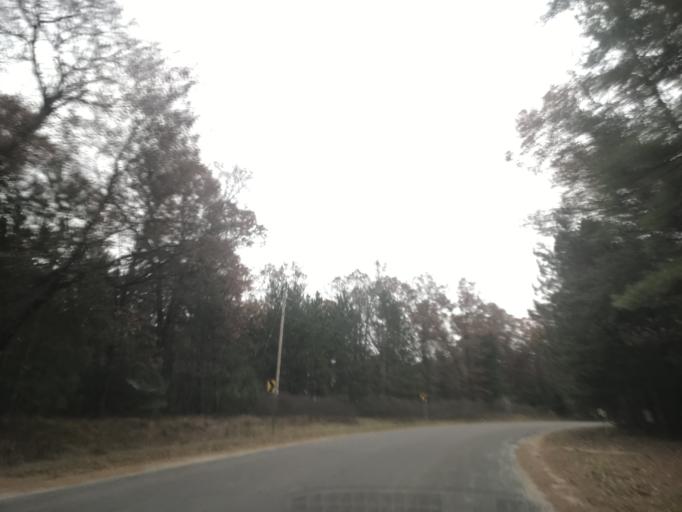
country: US
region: Wisconsin
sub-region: Oconto County
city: Gillett
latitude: 45.2690
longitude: -88.2542
